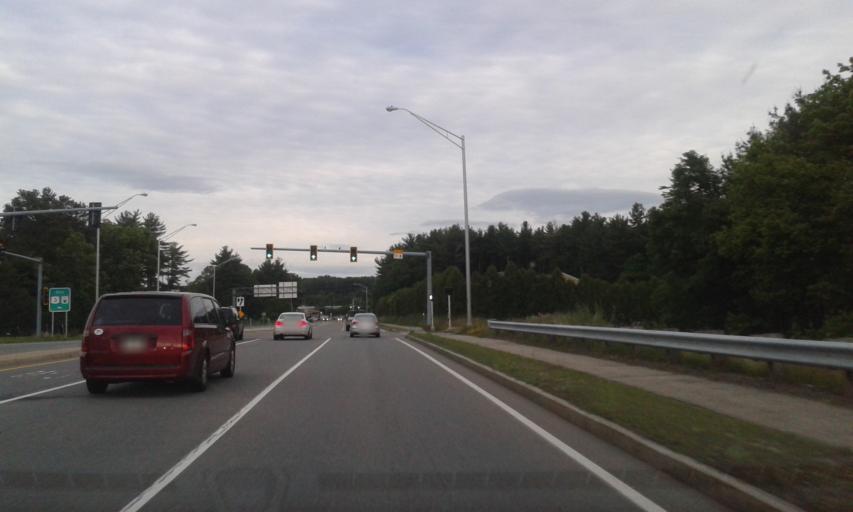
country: US
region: New Hampshire
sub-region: Hillsborough County
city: Nashua
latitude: 42.7456
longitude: -71.4954
